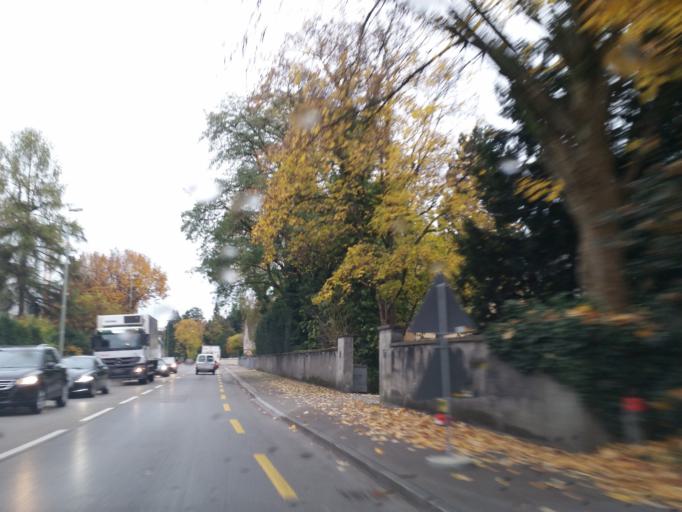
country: CH
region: Zurich
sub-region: Bezirk Meilen
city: Kuesnacht / Dorf
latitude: 47.3151
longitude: 8.5803
